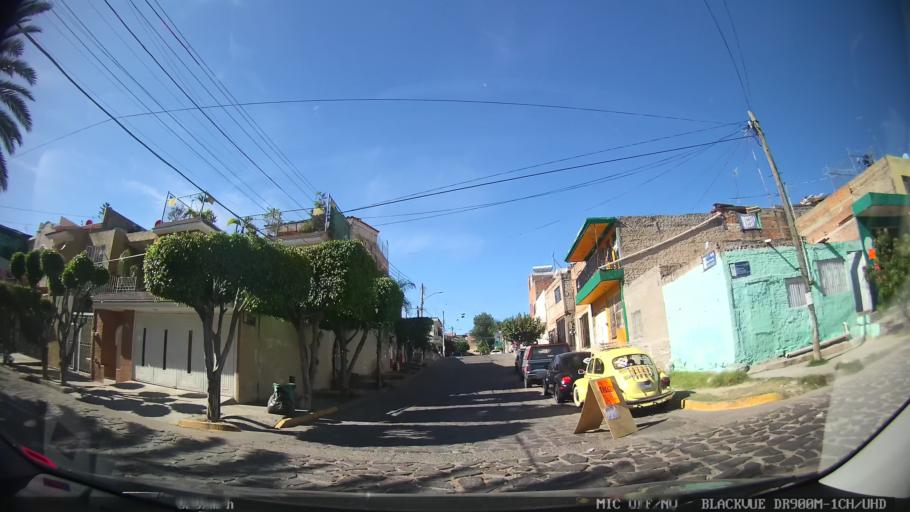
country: MX
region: Jalisco
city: Tlaquepaque
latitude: 20.6883
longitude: -103.2752
